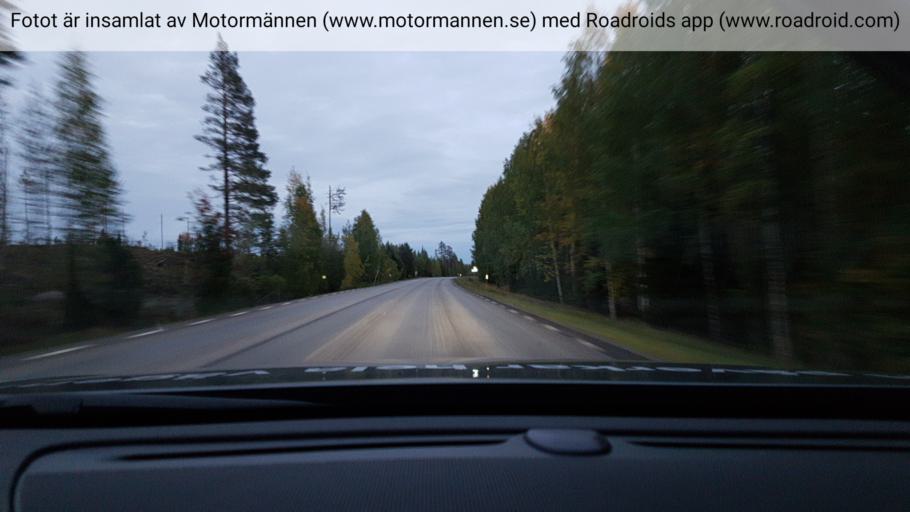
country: SE
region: Norrbotten
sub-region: Alvsbyns Kommun
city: AElvsbyn
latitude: 65.7769
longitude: 20.8418
